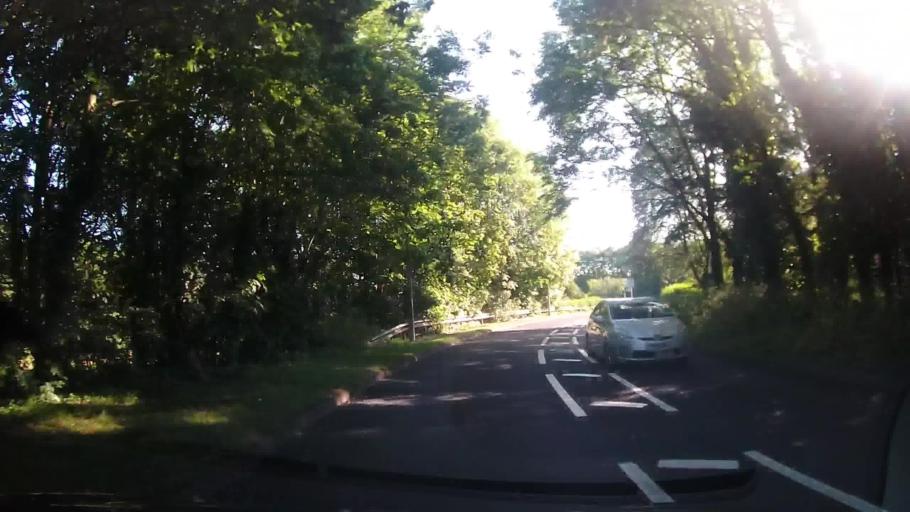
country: GB
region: England
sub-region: Shropshire
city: Hadley
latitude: 52.7072
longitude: -2.4938
